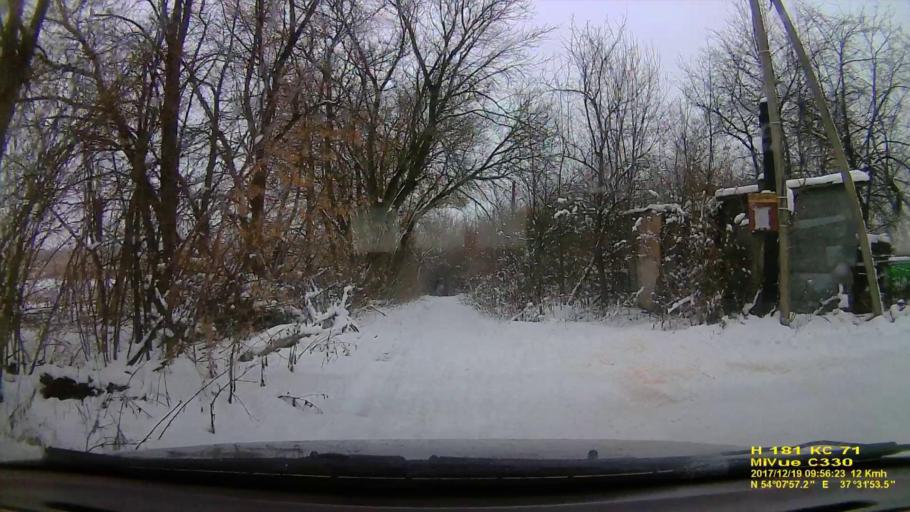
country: RU
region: Tula
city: Kosaya Gora
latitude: 54.1326
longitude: 37.5316
